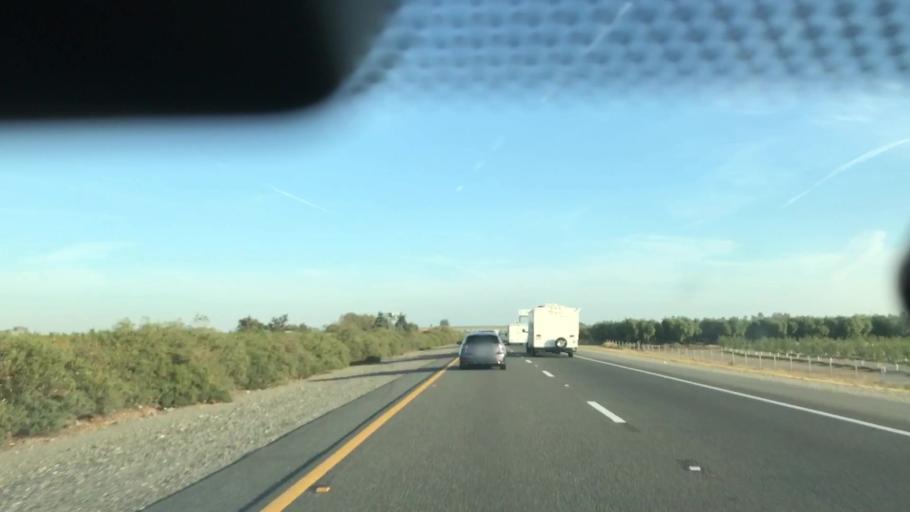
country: US
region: California
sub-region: Glenn County
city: Orland
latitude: 39.6921
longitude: -122.2049
